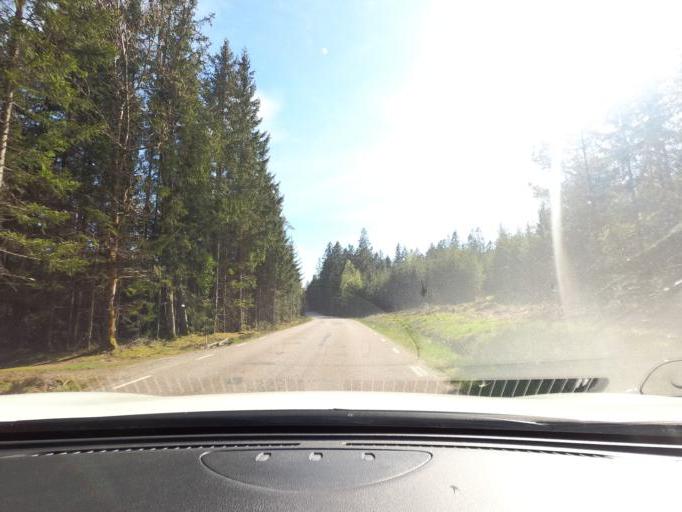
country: SE
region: Vaestra Goetaland
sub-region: Harryda Kommun
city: Hindas
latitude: 57.6352
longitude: 12.3355
